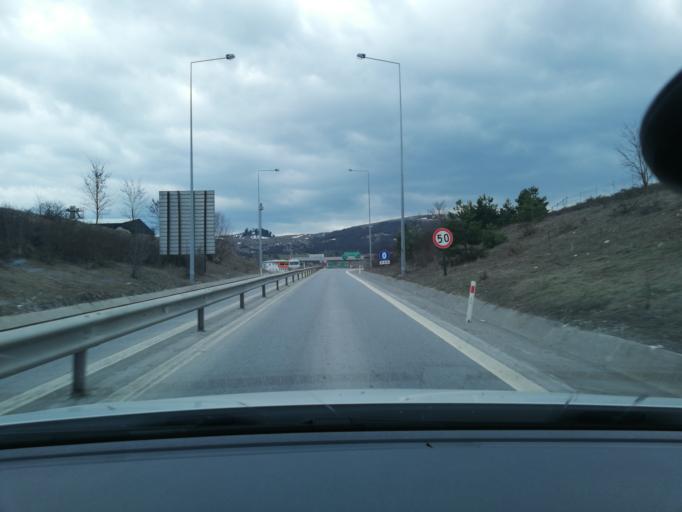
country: TR
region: Bolu
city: Yenicaga
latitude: 40.7704
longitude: 32.0082
